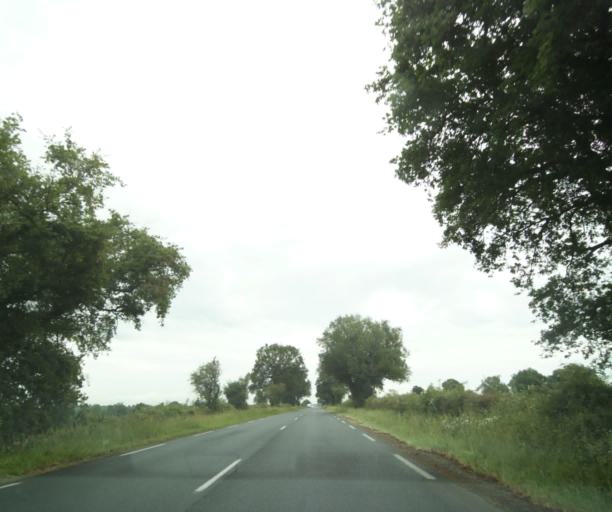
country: FR
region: Poitou-Charentes
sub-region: Departement des Deux-Sevres
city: Viennay
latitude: 46.7428
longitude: -0.2306
